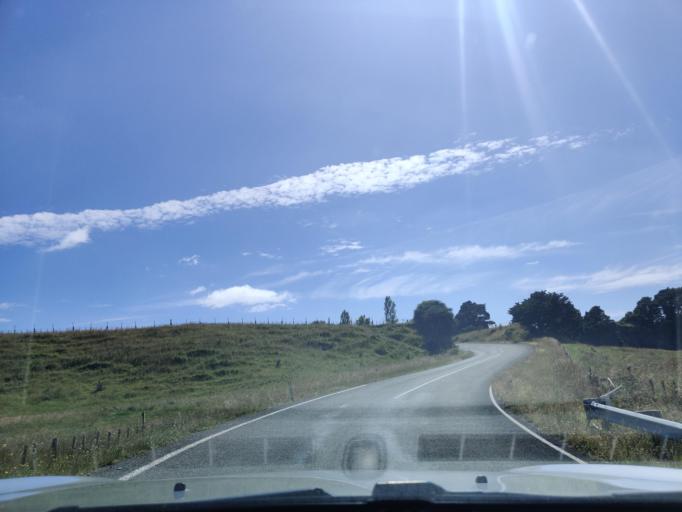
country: NZ
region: Manawatu-Wanganui
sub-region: Rangitikei District
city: Bulls
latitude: -40.1703
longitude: 175.4325
